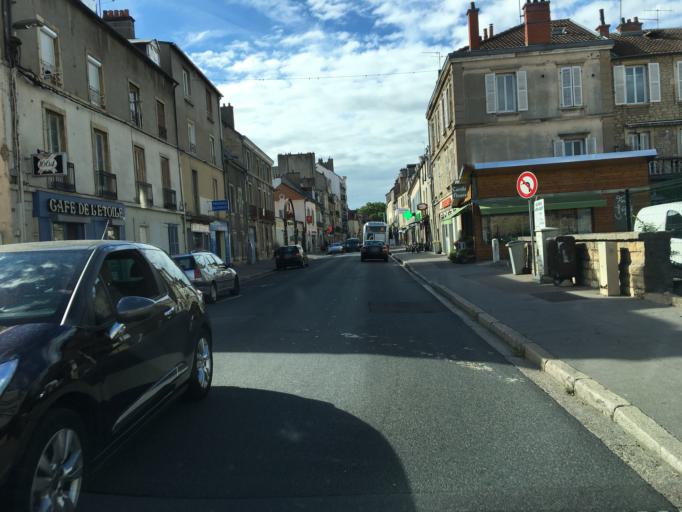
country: FR
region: Bourgogne
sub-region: Departement de la Cote-d'Or
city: Dijon
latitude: 47.3147
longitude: 5.0474
